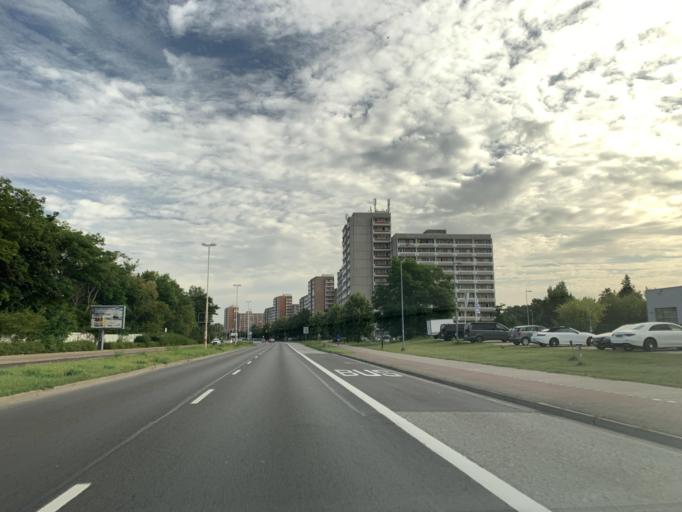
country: DE
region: Mecklenburg-Vorpommern
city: Neubrandenburg
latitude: 53.5393
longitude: 13.2646
